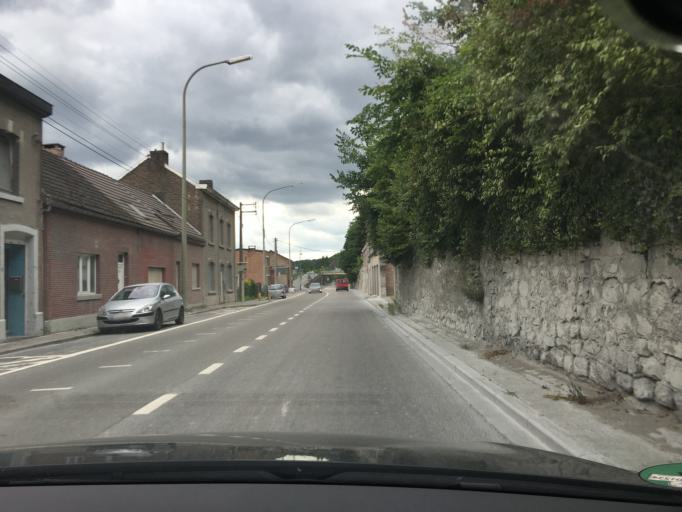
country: BE
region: Wallonia
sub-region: Province de Liege
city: Engis
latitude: 50.5660
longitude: 5.3581
